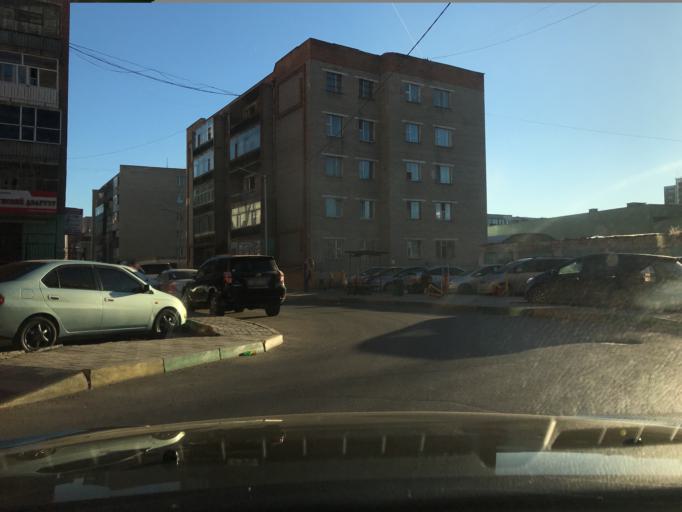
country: MN
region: Ulaanbaatar
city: Ulaanbaatar
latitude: 47.9282
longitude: 106.9110
